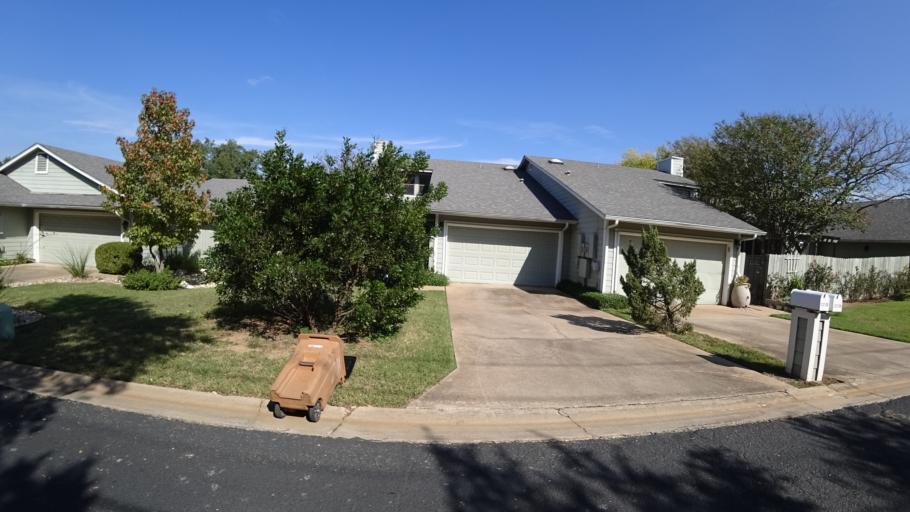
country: US
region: Texas
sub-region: Travis County
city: Shady Hollow
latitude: 30.2119
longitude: -97.8274
